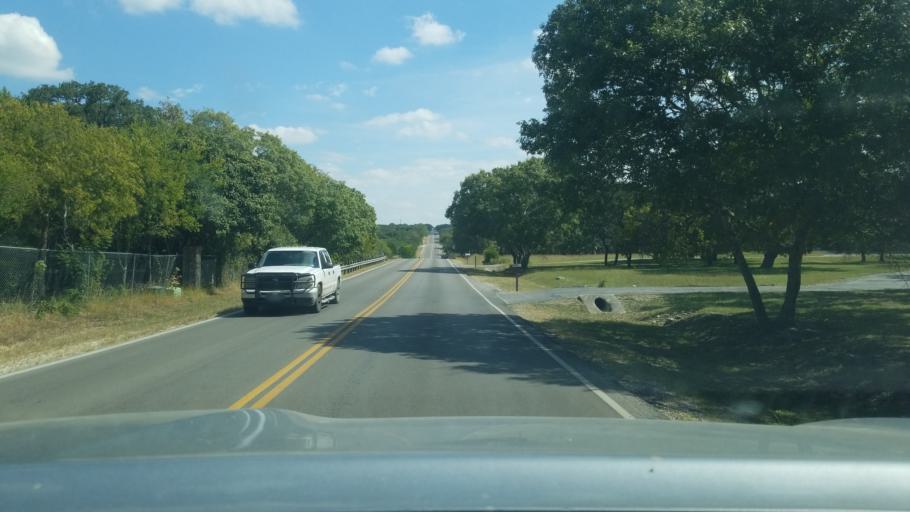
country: US
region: Texas
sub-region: Bexar County
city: Fair Oaks Ranch
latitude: 29.7311
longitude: -98.6531
